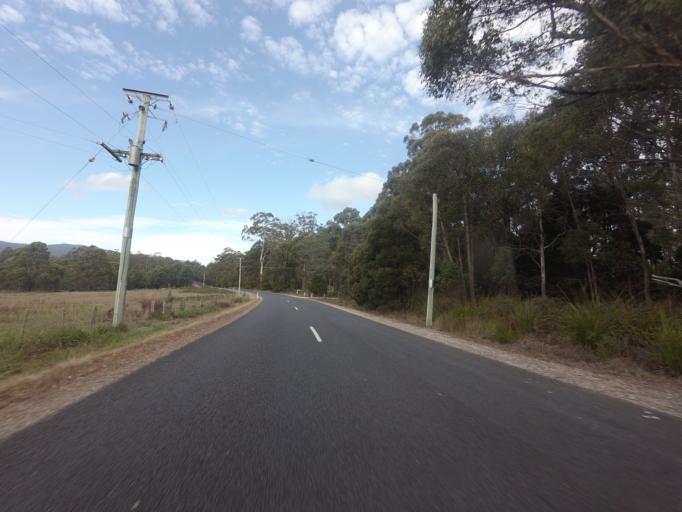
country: AU
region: Tasmania
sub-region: Meander Valley
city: Deloraine
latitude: -41.6175
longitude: 146.6928
